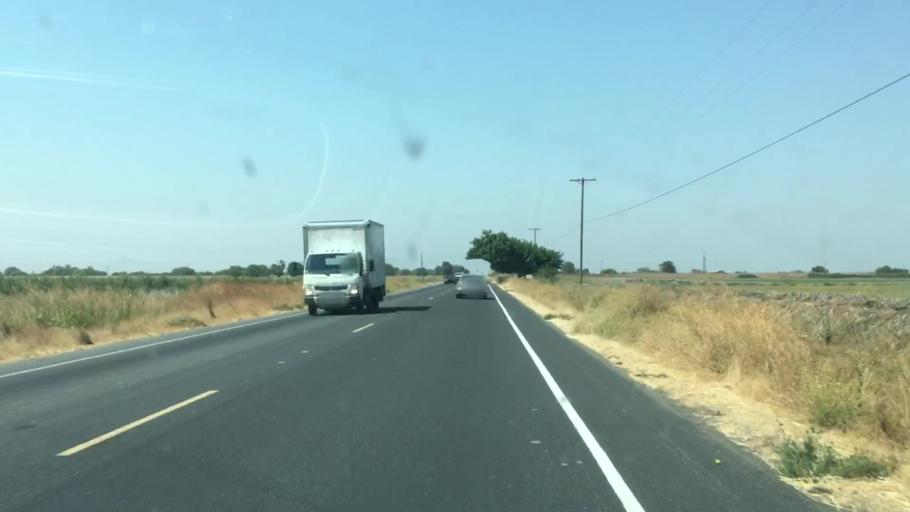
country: US
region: California
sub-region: San Joaquin County
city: Tracy
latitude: 37.8509
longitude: -121.4400
